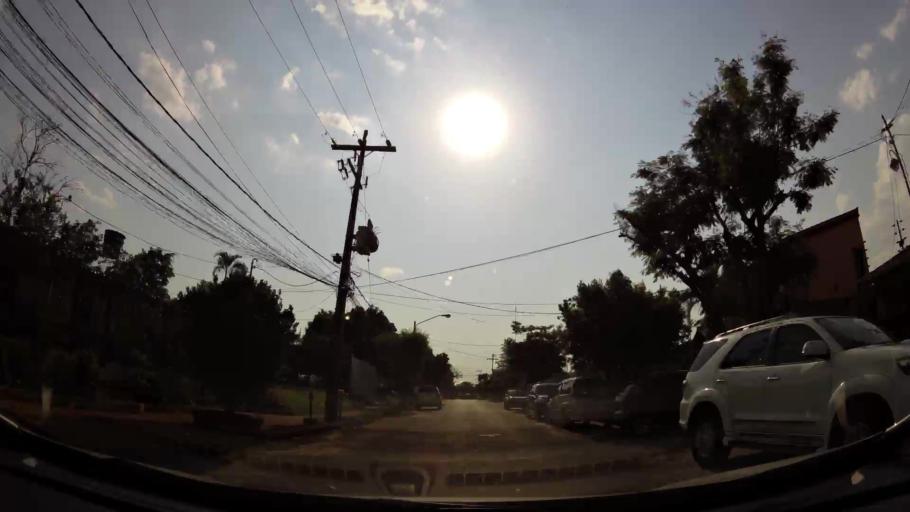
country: PY
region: Alto Parana
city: Presidente Franco
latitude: -25.5308
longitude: -54.6250
